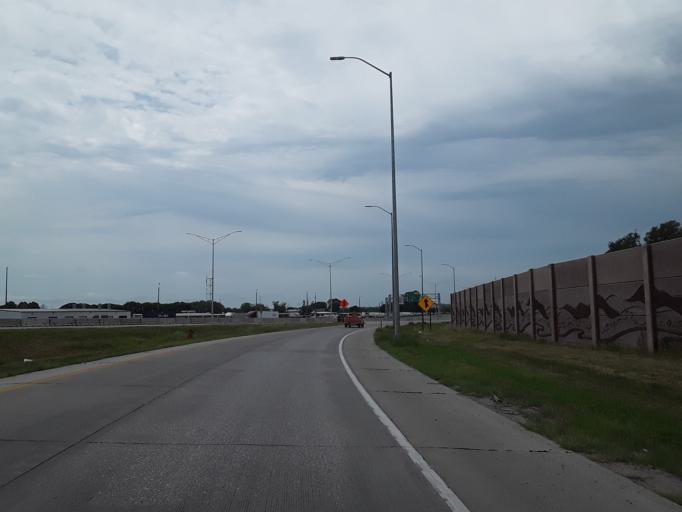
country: US
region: Iowa
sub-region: Pottawattamie County
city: Council Bluffs
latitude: 41.2330
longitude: -95.8557
